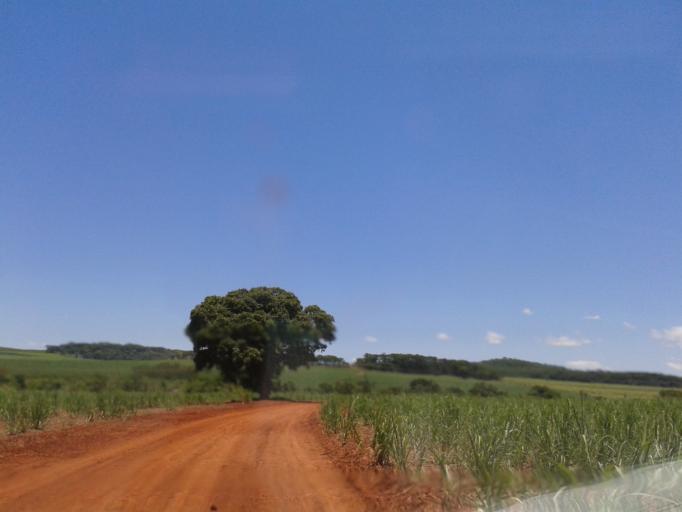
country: BR
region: Minas Gerais
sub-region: Centralina
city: Centralina
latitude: -18.6650
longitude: -49.2338
